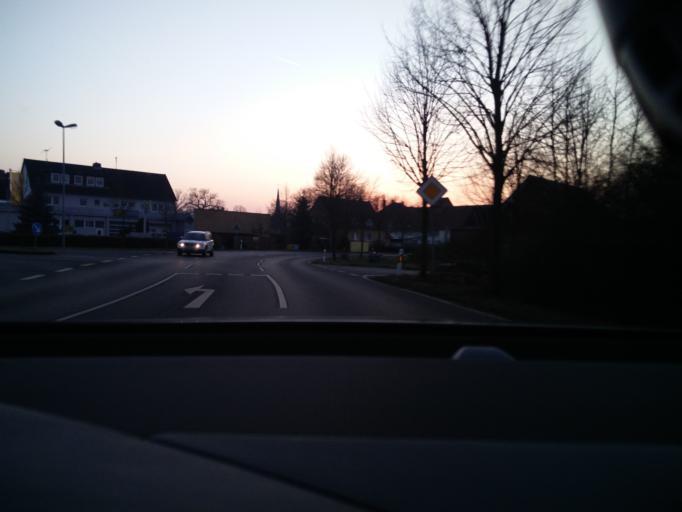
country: DE
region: Lower Saxony
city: Sehnde
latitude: 52.3209
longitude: 9.9346
